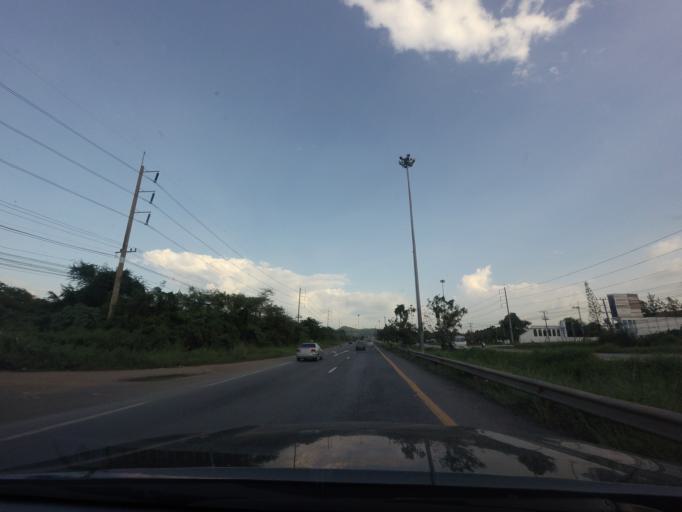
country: TH
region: Sara Buri
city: Saraburi
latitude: 14.5044
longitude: 100.9128
